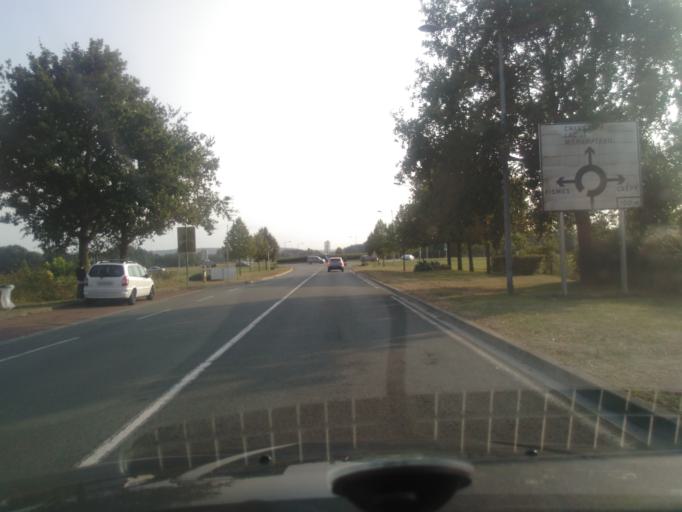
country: FR
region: Picardie
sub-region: Departement de l'Aisne
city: Laon
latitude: 49.5492
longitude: 3.6021
